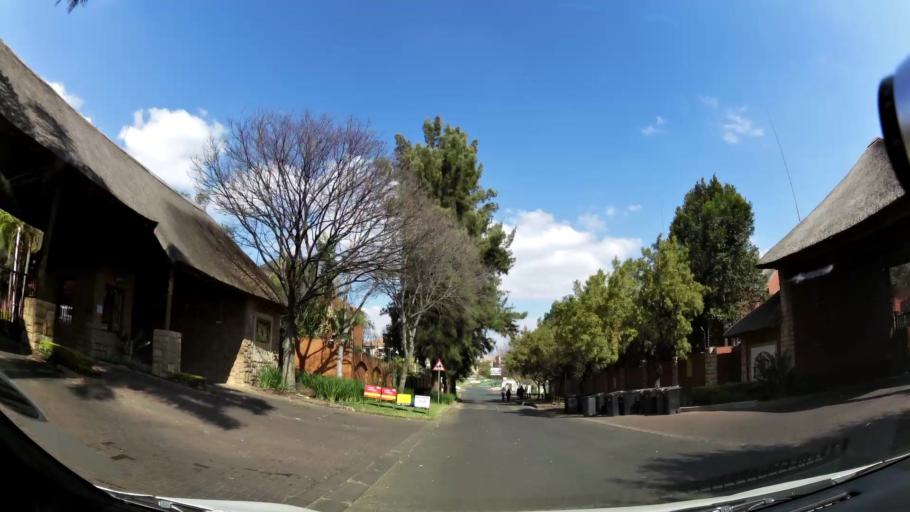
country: ZA
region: Gauteng
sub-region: City of Johannesburg Metropolitan Municipality
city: Midrand
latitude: -26.0288
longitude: 28.0667
